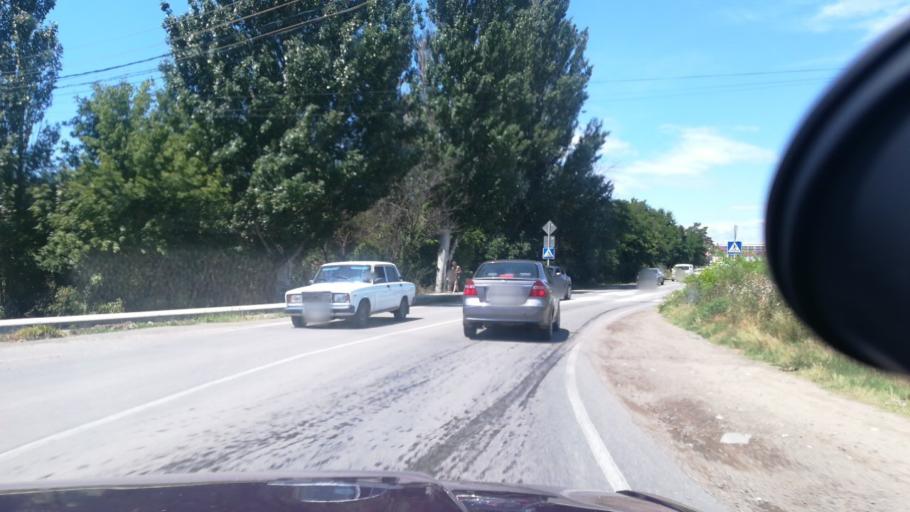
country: RU
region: Krasnodarskiy
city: Vityazevo
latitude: 44.9593
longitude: 37.2965
